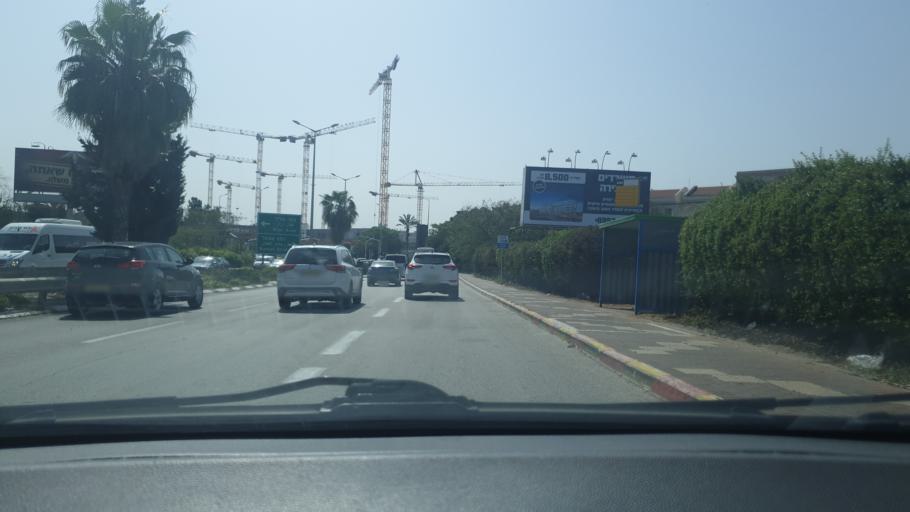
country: IL
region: Tel Aviv
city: Bene Beraq
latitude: 32.0531
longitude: 34.8365
